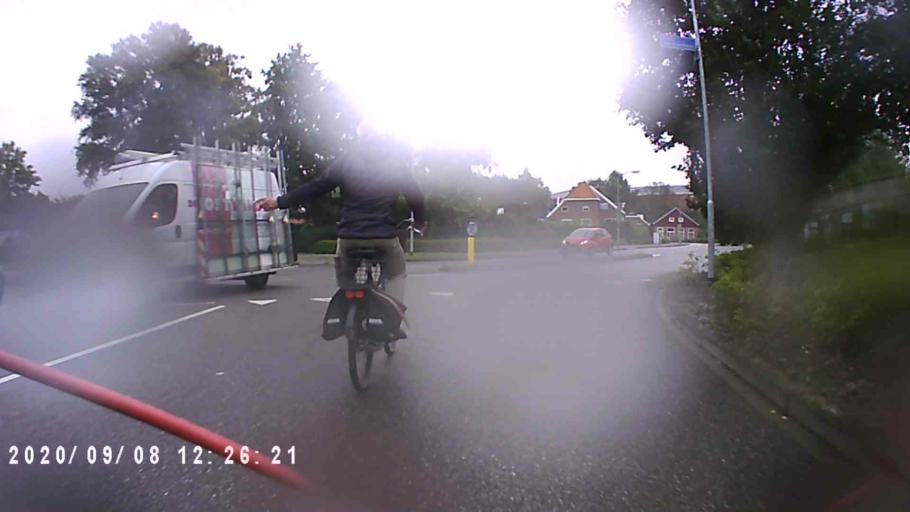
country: NL
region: Groningen
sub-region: Gemeente Veendam
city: Veendam
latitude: 53.0968
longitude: 6.8723
